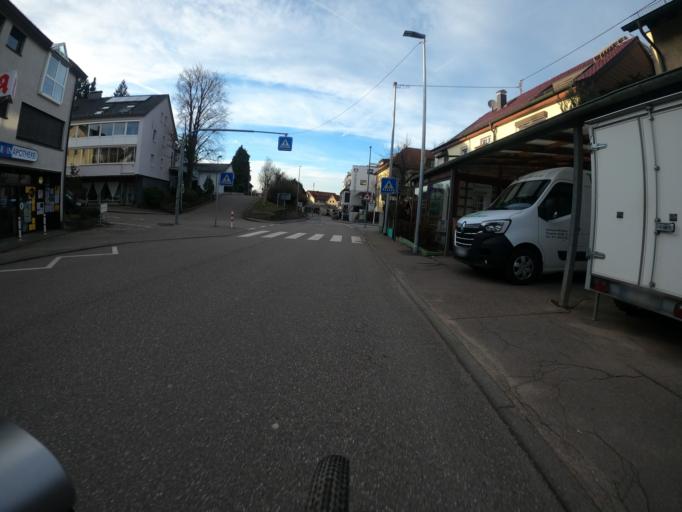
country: DE
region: Baden-Wuerttemberg
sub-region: Regierungsbezirk Stuttgart
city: Denkendorf
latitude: 48.7177
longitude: 9.3196
